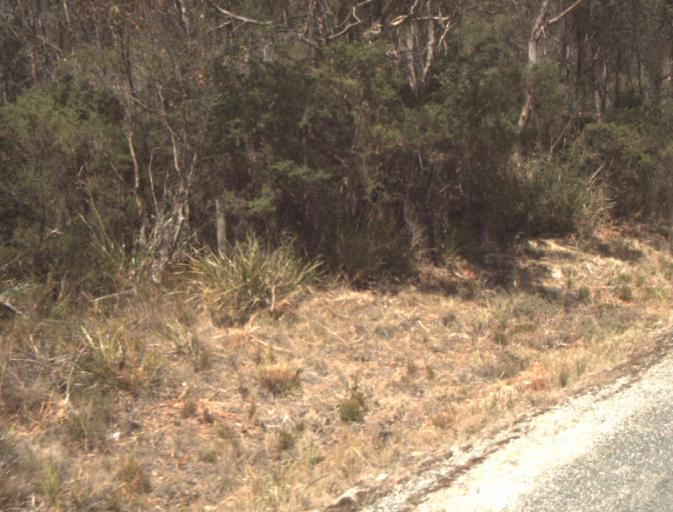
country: AU
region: Tasmania
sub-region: Launceston
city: Mayfield
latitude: -41.3539
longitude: 147.1437
